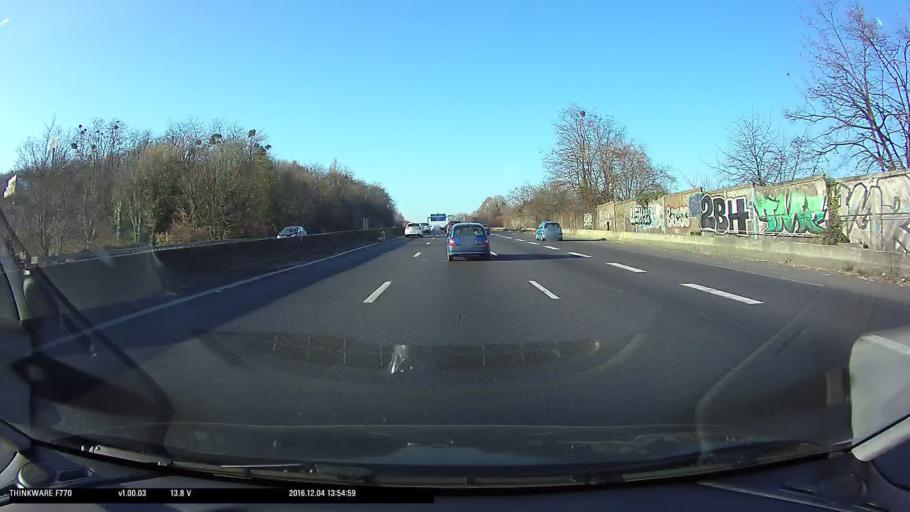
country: FR
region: Ile-de-France
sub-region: Departement du Val-d'Oise
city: Franconville
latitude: 48.9781
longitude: 2.2315
